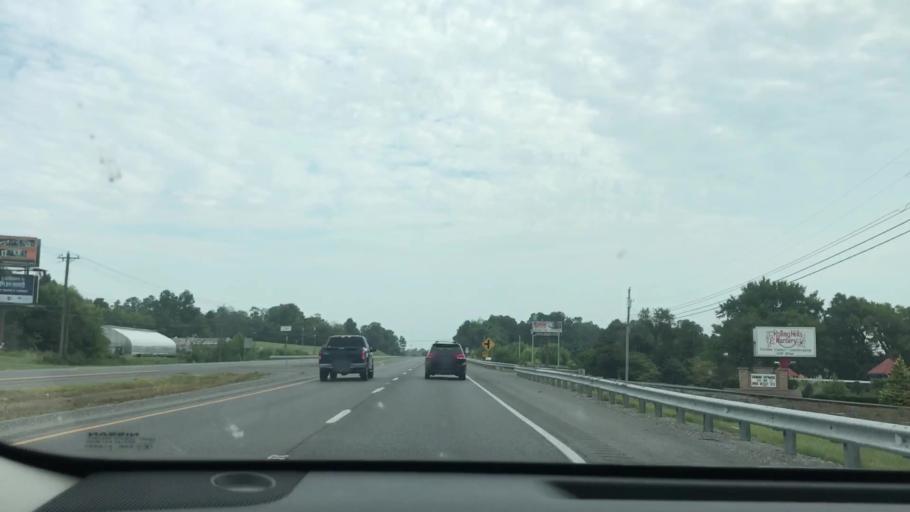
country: US
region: Kentucky
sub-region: Calloway County
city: Murray
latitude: 36.6651
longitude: -88.3044
